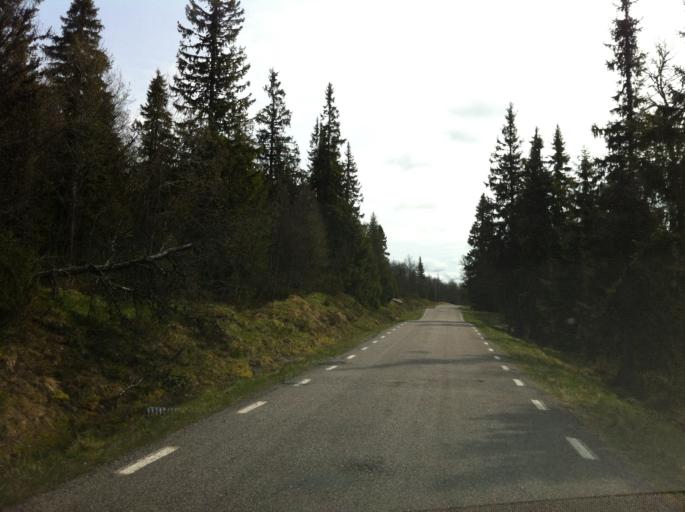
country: NO
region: Hedmark
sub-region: Engerdal
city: Engerdal
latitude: 62.2984
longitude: 12.8040
